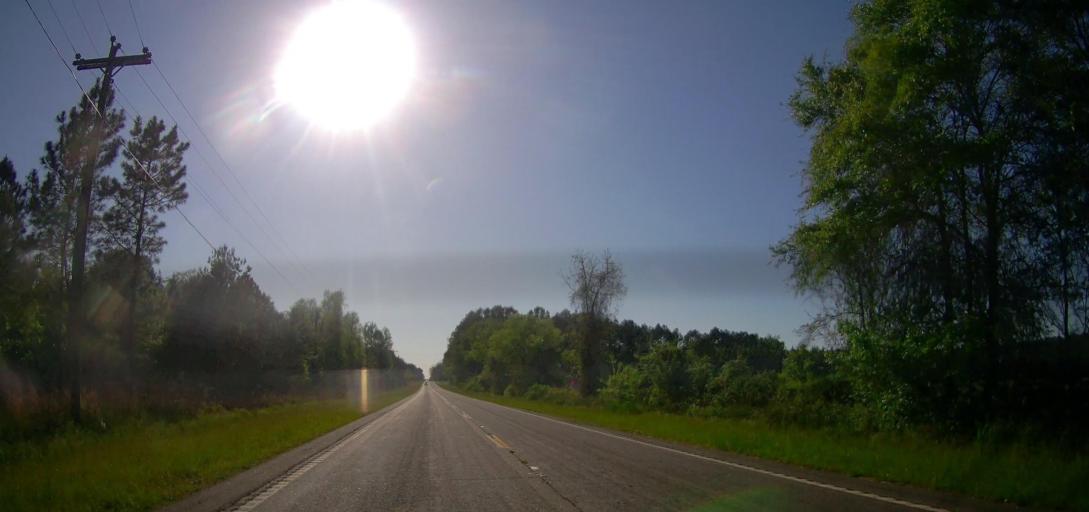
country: US
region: Georgia
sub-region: Ben Hill County
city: Fitzgerald
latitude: 31.7183
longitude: -83.3275
